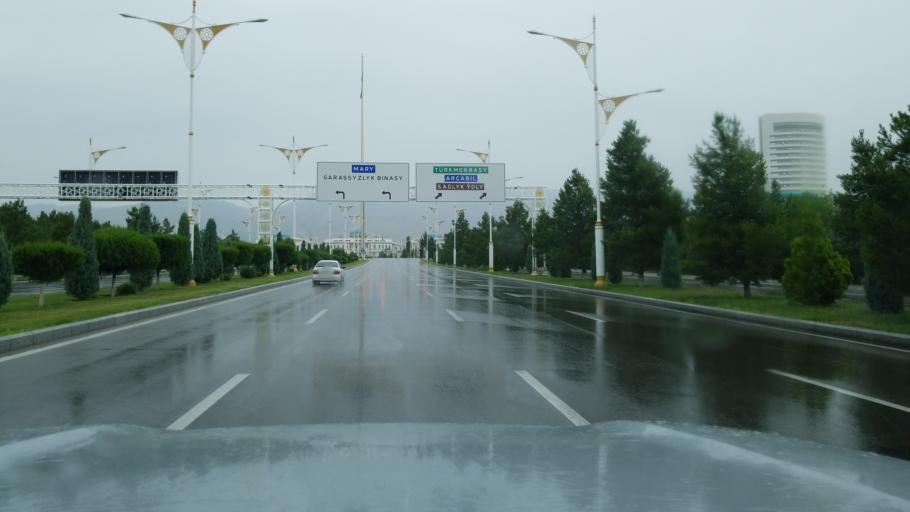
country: TM
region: Ahal
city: Ashgabat
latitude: 37.8904
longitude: 58.3533
